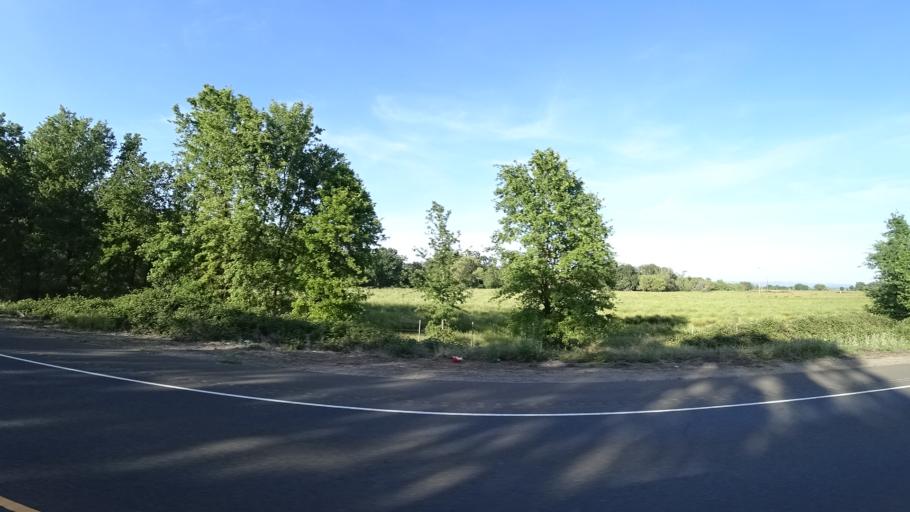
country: US
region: California
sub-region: Placer County
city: Sheridan
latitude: 38.9364
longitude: -121.3492
